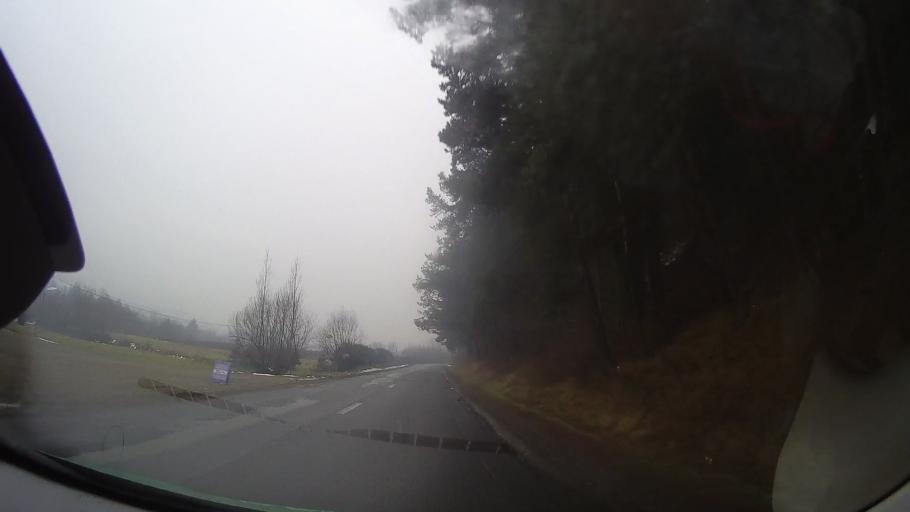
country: RO
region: Harghita
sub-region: Municipiul Gheorgheni
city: Gheorgheni
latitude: 46.7324
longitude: 25.6468
